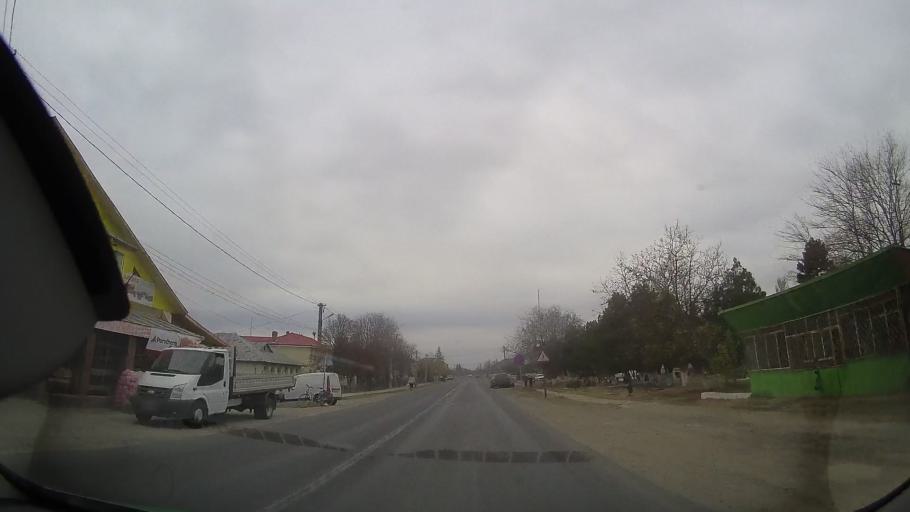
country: RO
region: Buzau
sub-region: Comuna Padina
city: Padina
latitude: 44.8299
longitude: 27.1135
